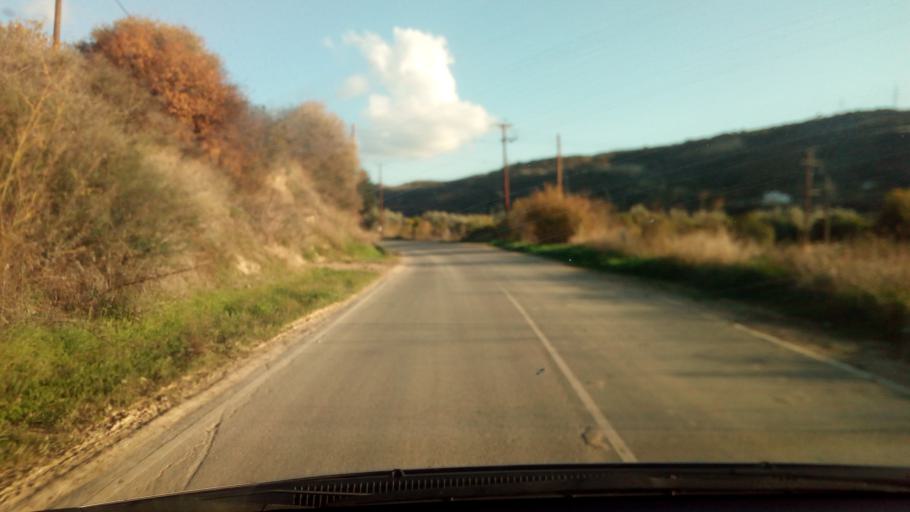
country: CY
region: Pafos
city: Polis
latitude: 34.9812
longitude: 32.4581
